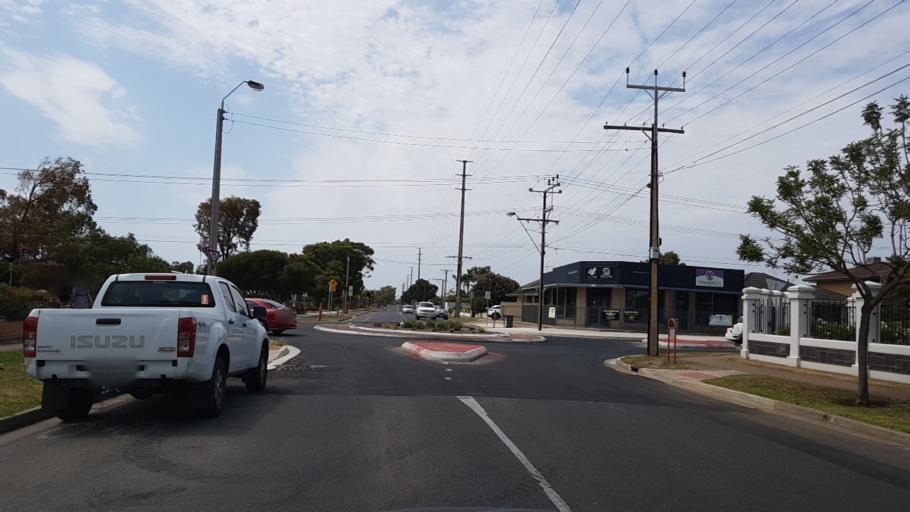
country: AU
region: South Australia
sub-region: Charles Sturt
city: Henley Beach
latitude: -34.9137
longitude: 138.5045
